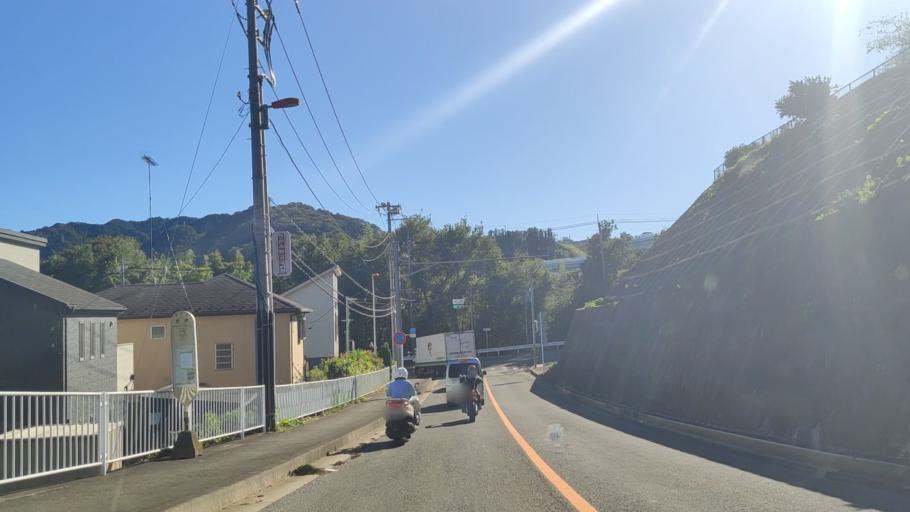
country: JP
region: Tokyo
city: Hachioji
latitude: 35.5849
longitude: 139.2960
